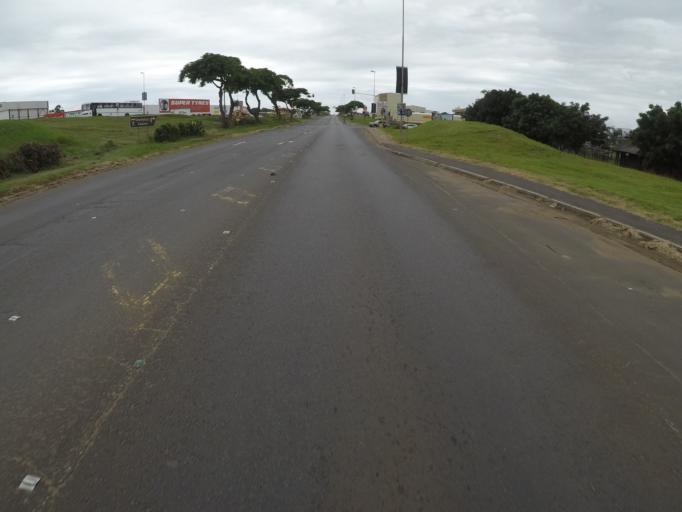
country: ZA
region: KwaZulu-Natal
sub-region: uThungulu District Municipality
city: Empangeni
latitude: -28.7737
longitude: 31.9013
